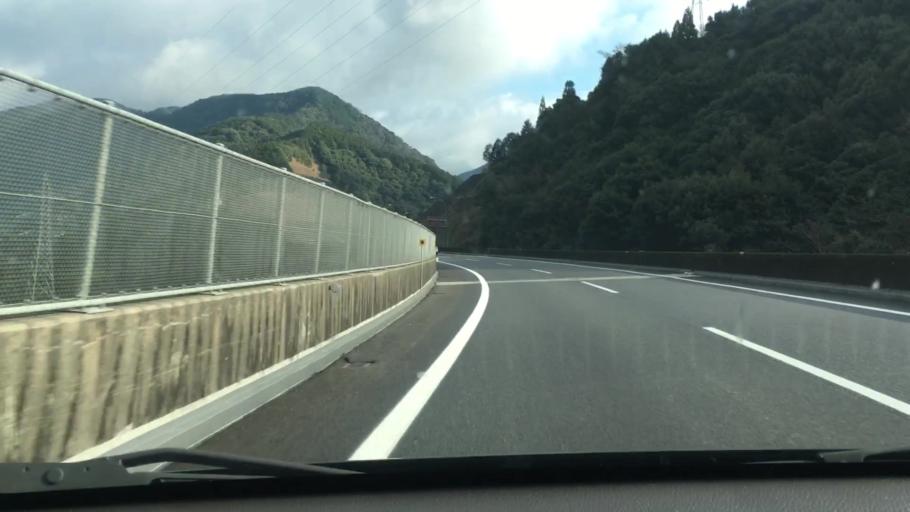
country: JP
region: Kumamoto
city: Yatsushiro
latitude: 32.4440
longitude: 130.6648
